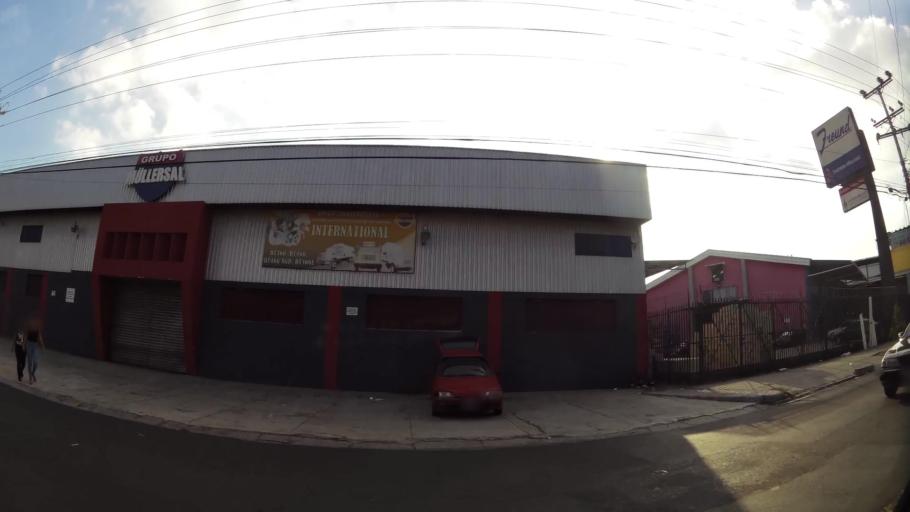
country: SV
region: San Salvador
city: San Salvador
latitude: 13.6923
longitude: -89.2184
